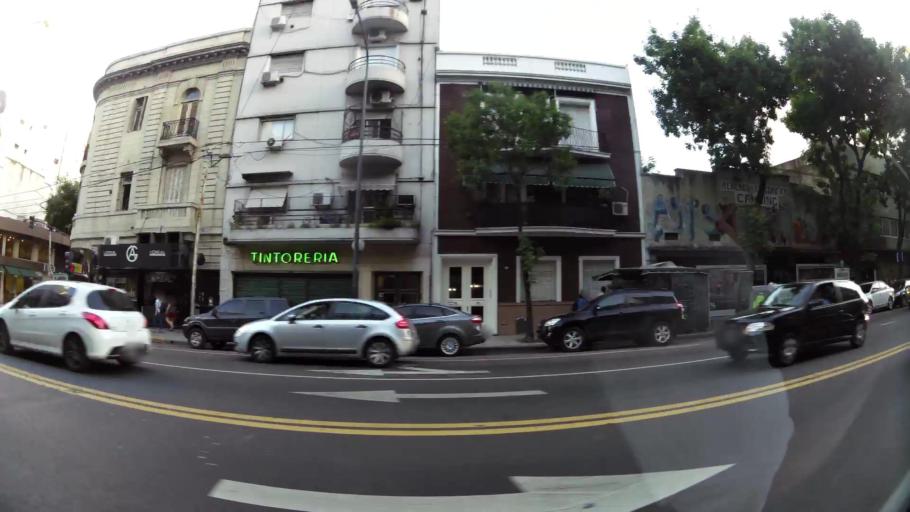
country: AR
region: Buenos Aires F.D.
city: Colegiales
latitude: -34.5862
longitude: -58.4177
